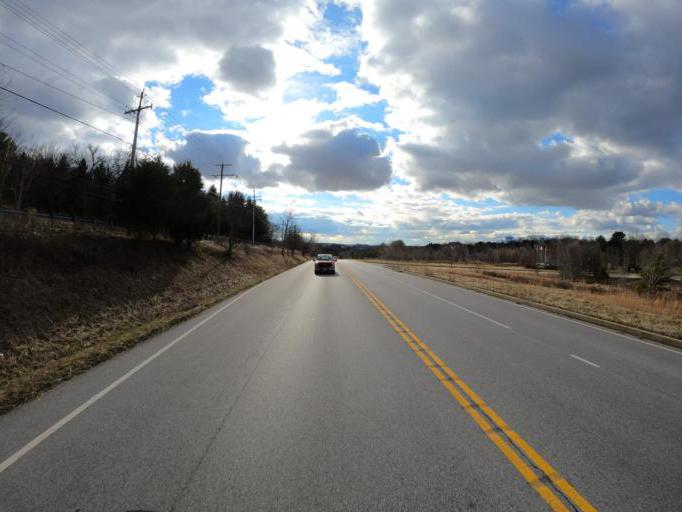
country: US
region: Maryland
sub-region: Carroll County
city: Westminster
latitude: 39.5647
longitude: -77.0244
